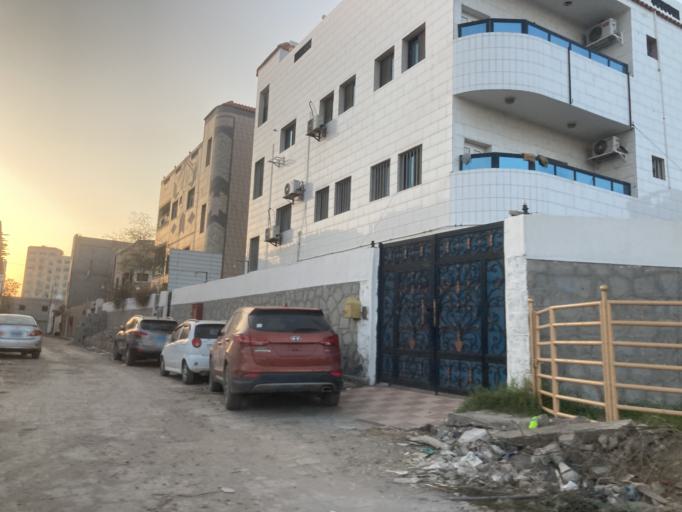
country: YE
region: Aden
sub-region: Al Mansura
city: Al Mansurah
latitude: 12.8529
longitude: 44.9914
